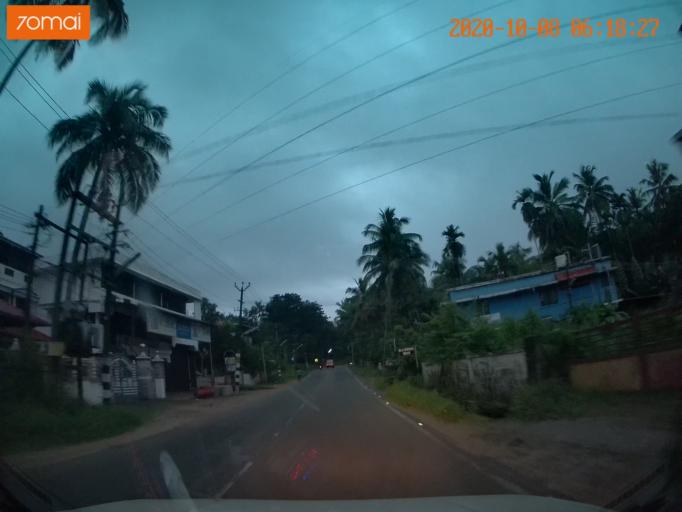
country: IN
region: Kerala
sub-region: Thrissur District
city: Trichur
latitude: 10.5123
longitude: 76.2472
